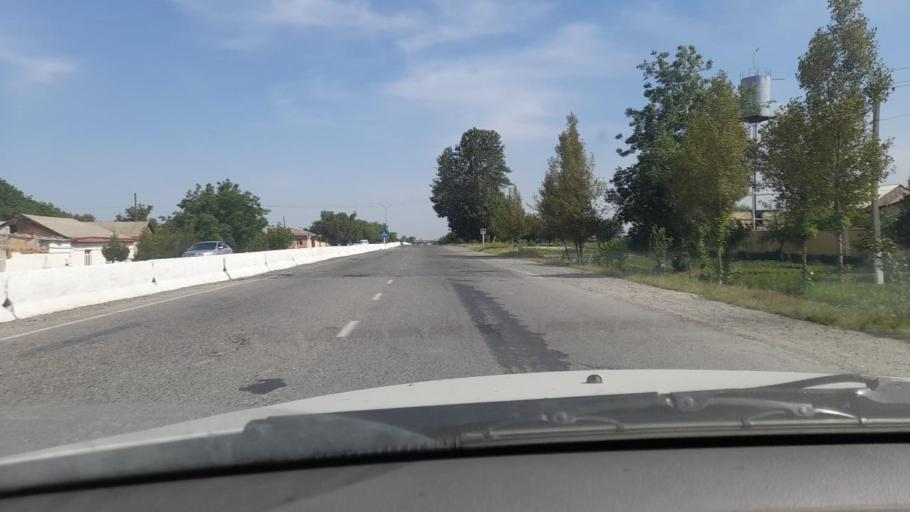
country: UZ
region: Samarqand
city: Daxbet
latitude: 39.7785
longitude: 66.8888
